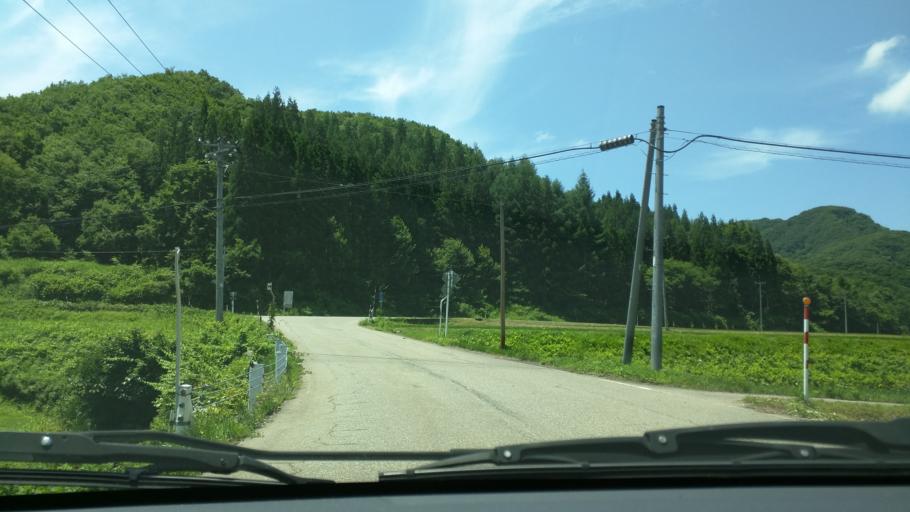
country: JP
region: Tochigi
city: Kuroiso
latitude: 37.2547
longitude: 139.7692
